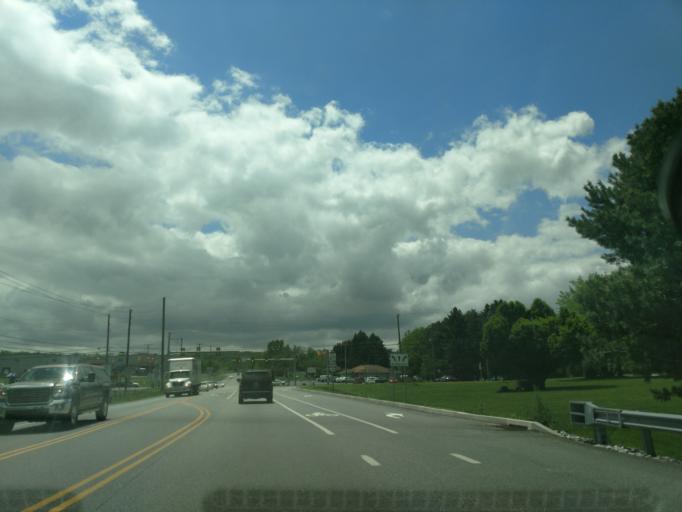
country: US
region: Pennsylvania
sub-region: Lebanon County
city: Cornwall
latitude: 40.2793
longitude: -76.4349
